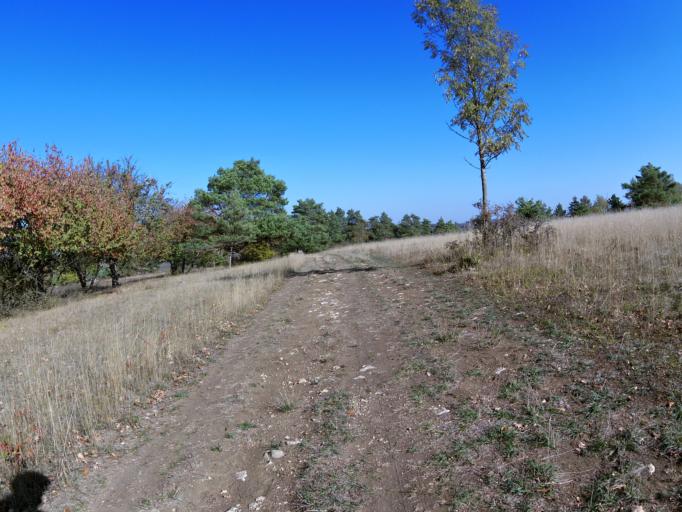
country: DE
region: Bavaria
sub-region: Regierungsbezirk Unterfranken
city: Eibelstadt
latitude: 49.7178
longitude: 9.9881
